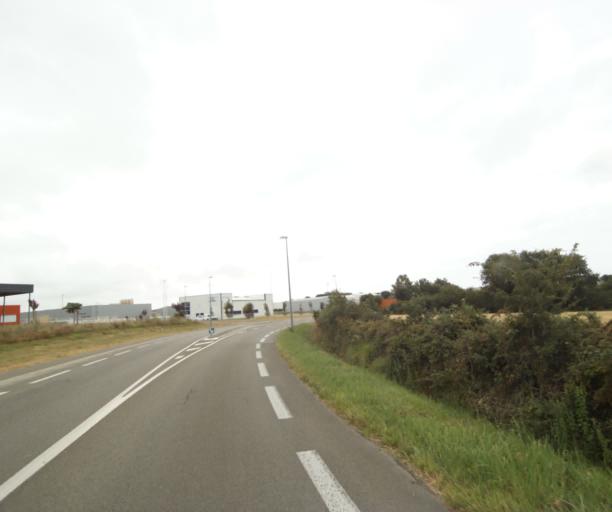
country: FR
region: Pays de la Loire
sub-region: Departement de la Vendee
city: Chateau-d'Olonne
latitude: 46.4955
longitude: -1.7324
